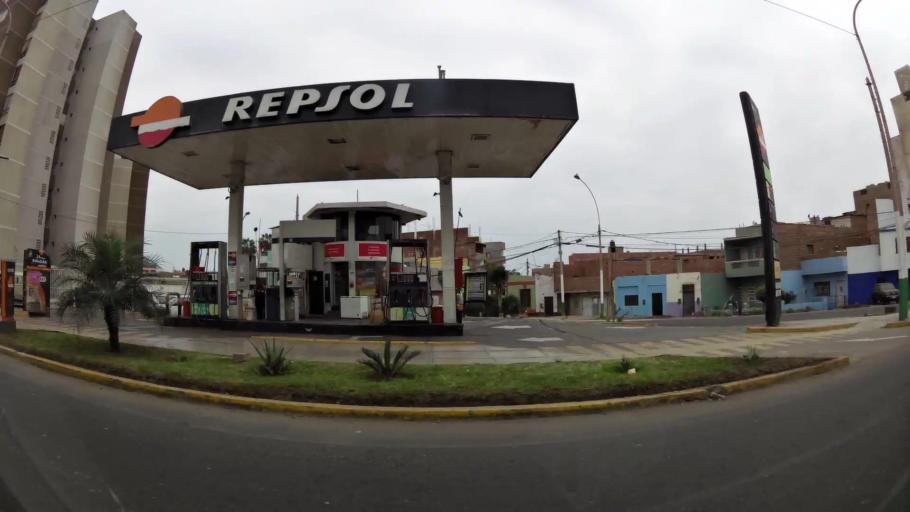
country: PE
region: Callao
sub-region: Callao
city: Callao
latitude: -12.0660
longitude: -77.1226
